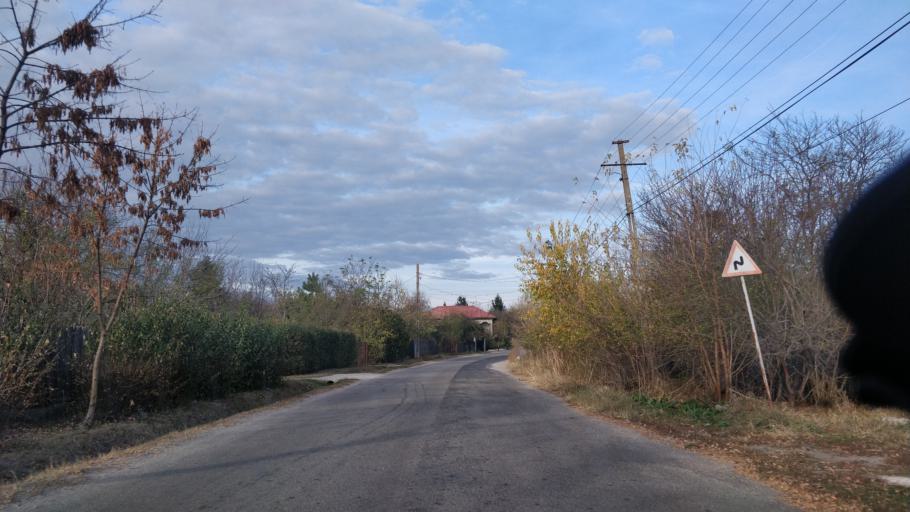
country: RO
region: Giurgiu
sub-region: Comuna Bucsani
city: Bucsani
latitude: 44.3498
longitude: 25.6552
